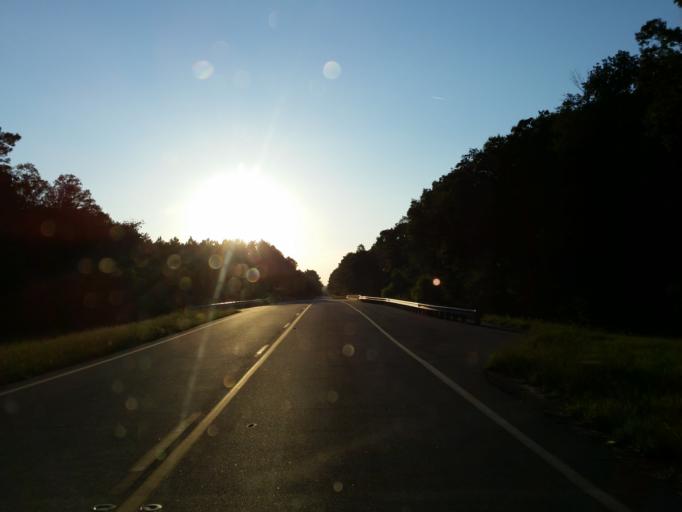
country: US
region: Georgia
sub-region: Berrien County
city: Ray City
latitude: 31.1732
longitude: -83.1140
